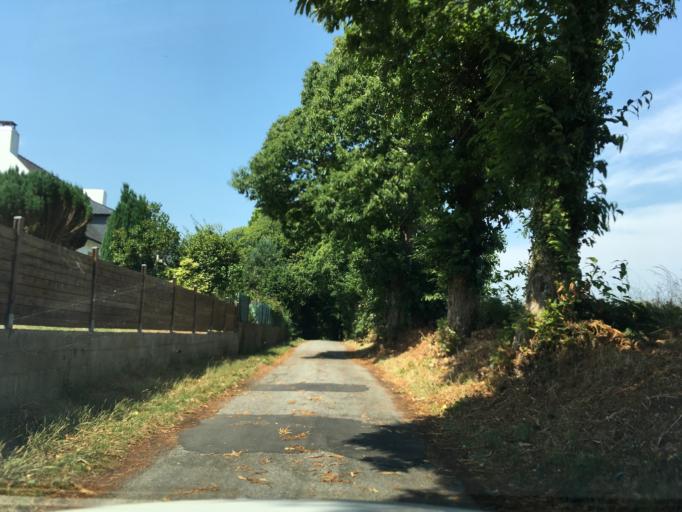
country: FR
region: Brittany
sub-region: Departement du Morbihan
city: Queven
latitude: 47.7689
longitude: -3.3985
